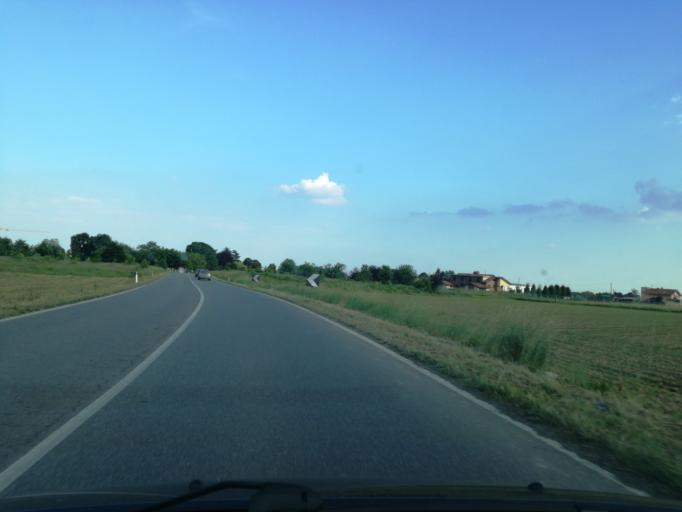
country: IT
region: Lombardy
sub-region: Provincia di Monza e Brianza
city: Cornate d'Adda
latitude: 45.6306
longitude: 9.4615
